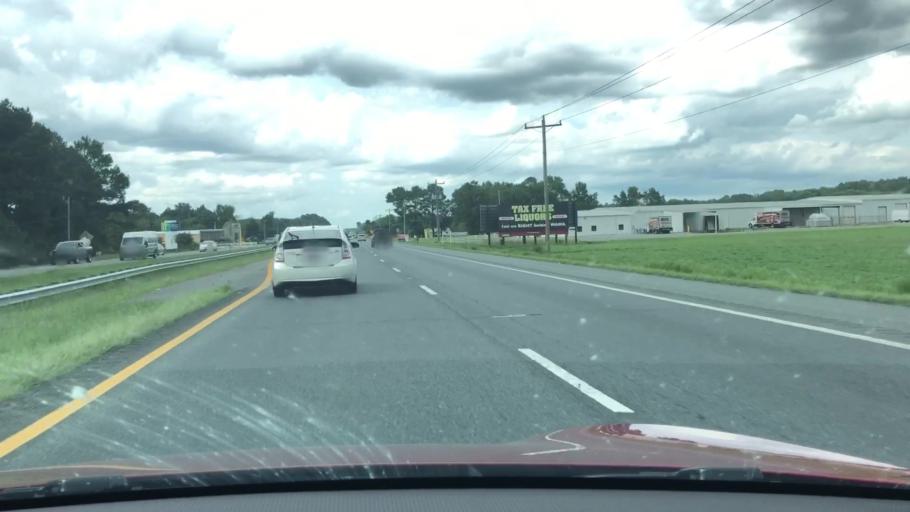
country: US
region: Maryland
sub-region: Wicomico County
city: Delmar
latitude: 38.4381
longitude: -75.5621
